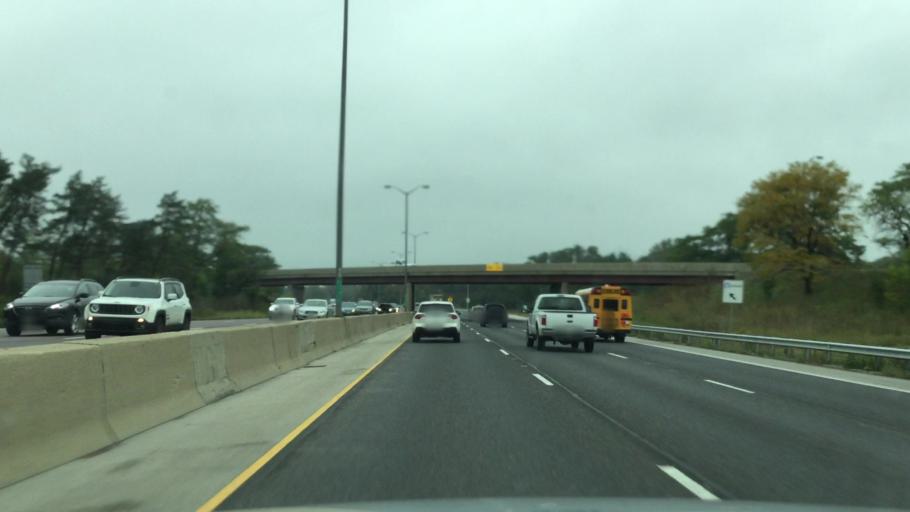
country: US
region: Illinois
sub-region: Cook County
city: Northfield
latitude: 42.0839
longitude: -87.7585
